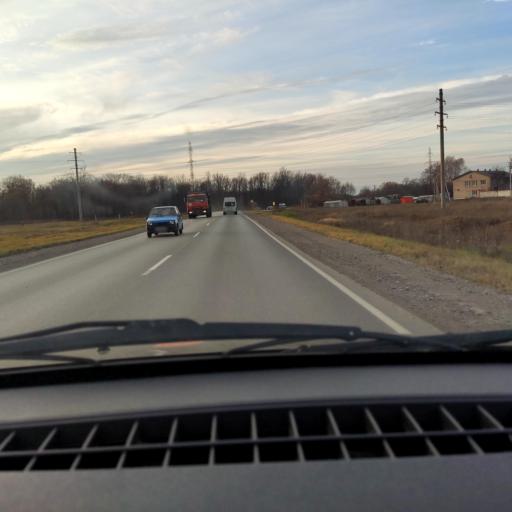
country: RU
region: Bashkortostan
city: Mikhaylovka
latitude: 54.8041
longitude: 55.8264
